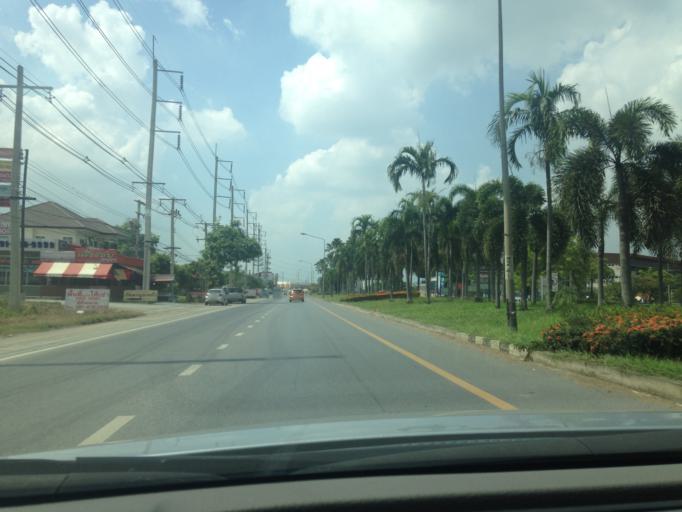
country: TH
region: Phra Nakhon Si Ayutthaya
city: Ban Bang Kadi Pathum Thani
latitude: 14.0028
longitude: 100.5673
